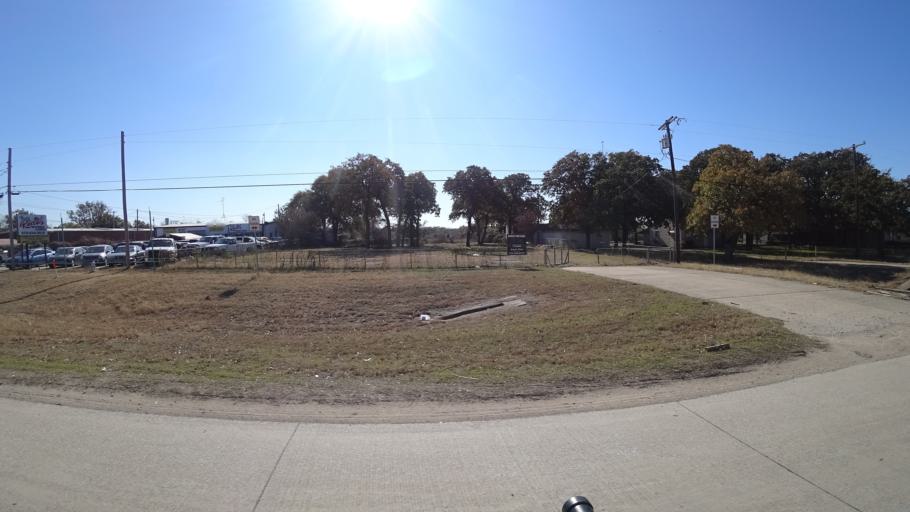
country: US
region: Texas
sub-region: Denton County
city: Lewisville
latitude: 33.0448
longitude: -96.9696
